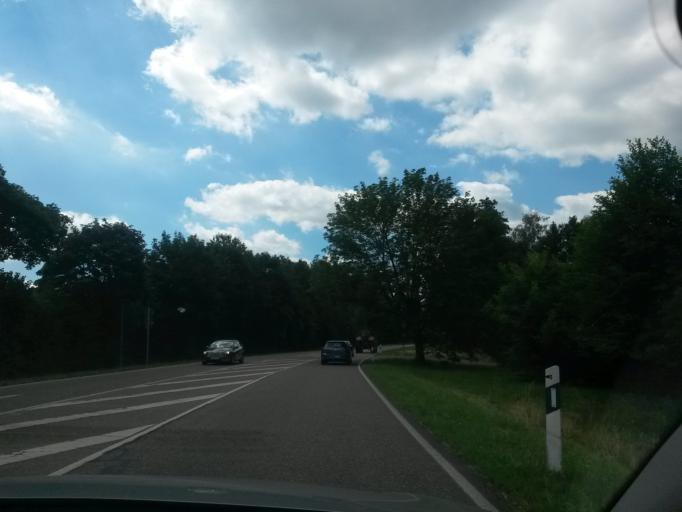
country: DE
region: Baden-Wuerttemberg
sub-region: Karlsruhe Region
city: Ettlingen
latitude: 48.9250
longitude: 8.3846
